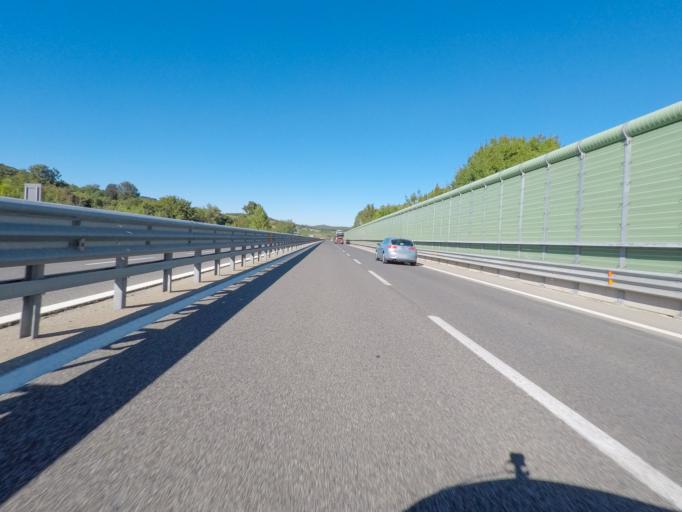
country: IT
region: Tuscany
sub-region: Provincia di Grosseto
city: Campagnatico
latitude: 42.8964
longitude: 11.2390
